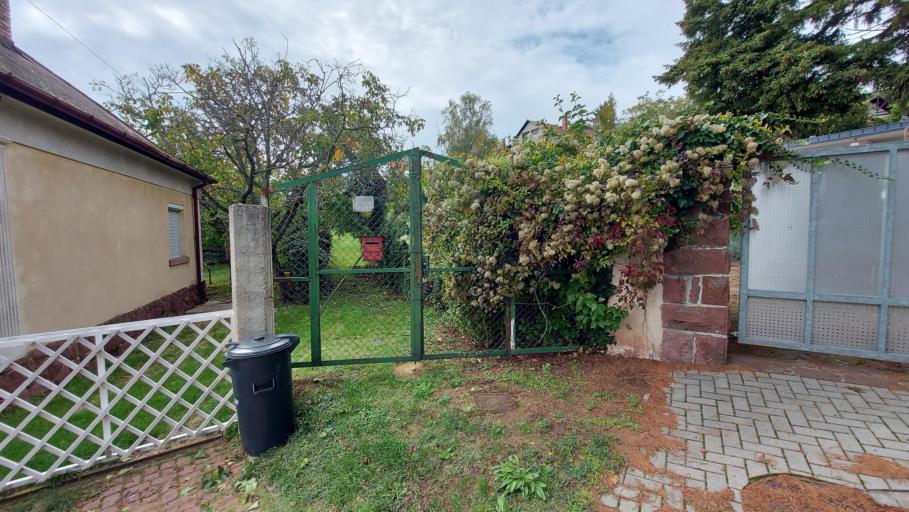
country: HU
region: Veszprem
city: Balatonalmadi
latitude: 47.0289
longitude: 18.0061
